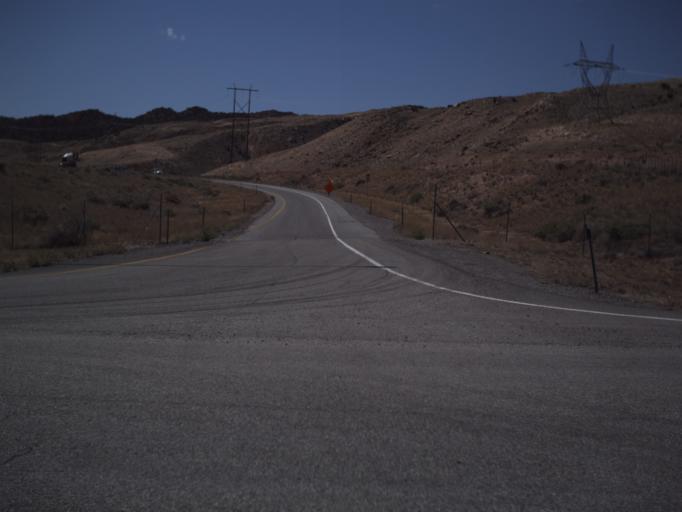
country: US
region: Utah
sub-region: Sevier County
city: Richfield
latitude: 38.7906
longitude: -112.0832
